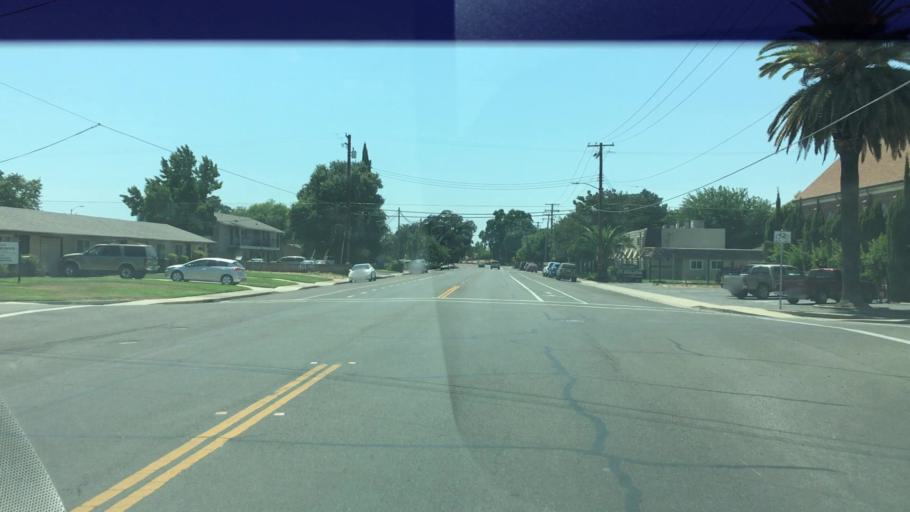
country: US
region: California
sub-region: Sacramento County
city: Galt
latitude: 38.2488
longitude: -121.3059
